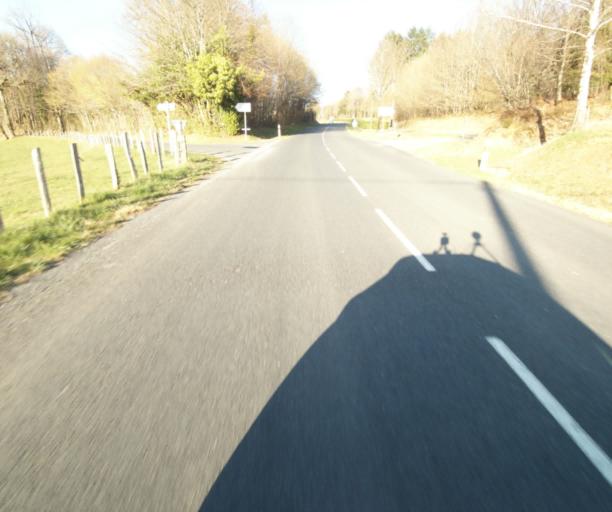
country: FR
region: Limousin
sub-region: Departement de la Correze
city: Seilhac
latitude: 45.3527
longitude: 1.7051
